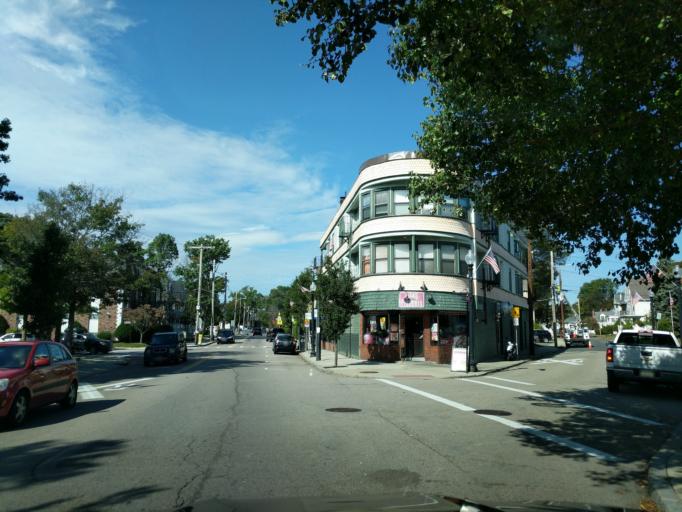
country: US
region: Massachusetts
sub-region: Middlesex County
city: Melrose
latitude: 42.4521
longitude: -71.0694
